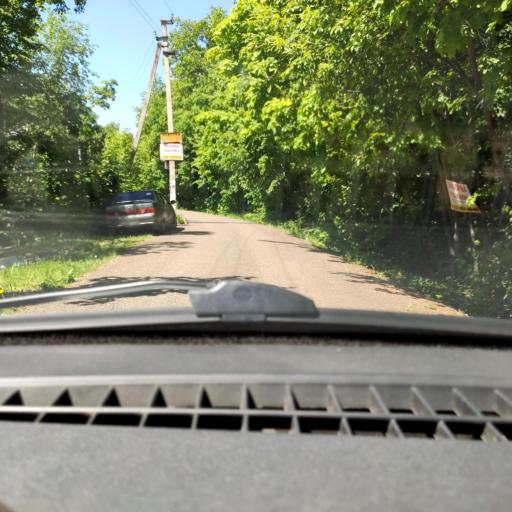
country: RU
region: Bashkortostan
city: Kabakovo
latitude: 54.4296
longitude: 55.9151
